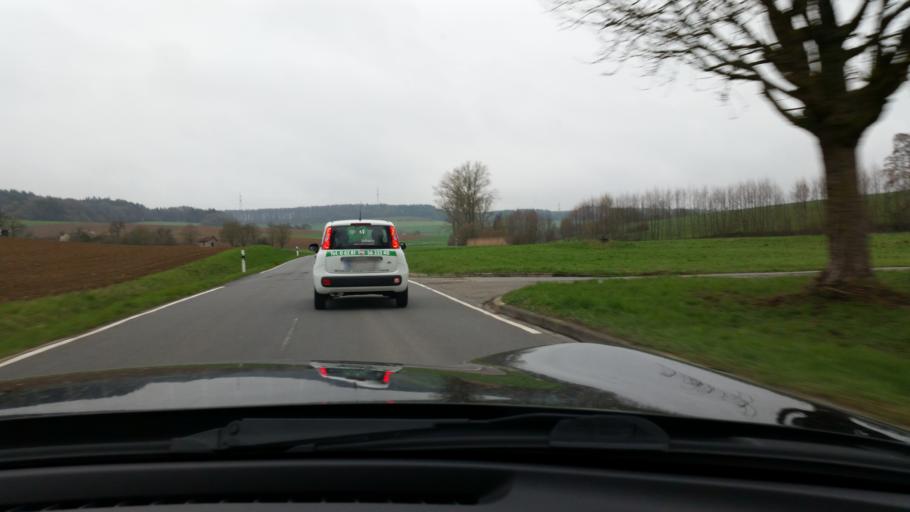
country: DE
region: Baden-Wuerttemberg
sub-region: Karlsruhe Region
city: Buchen
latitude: 49.5001
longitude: 9.3908
